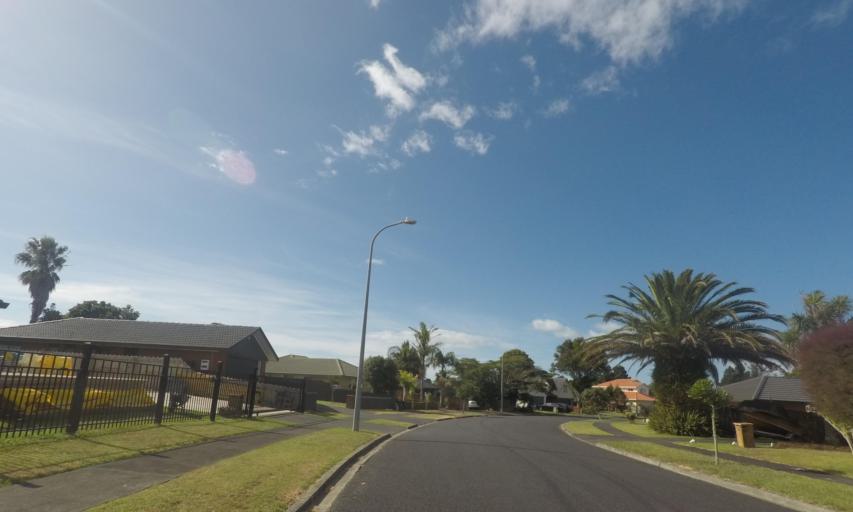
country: NZ
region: Auckland
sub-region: Auckland
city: Pakuranga
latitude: -36.9227
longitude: 174.8919
